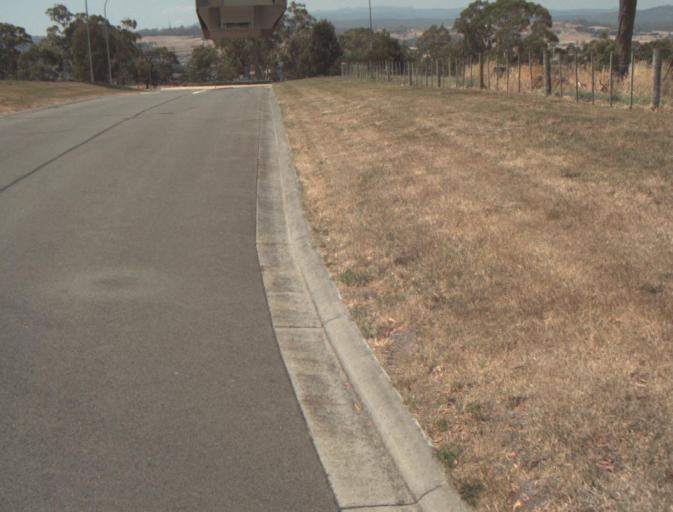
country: AU
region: Tasmania
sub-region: Launceston
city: Newstead
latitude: -41.4740
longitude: 147.1742
